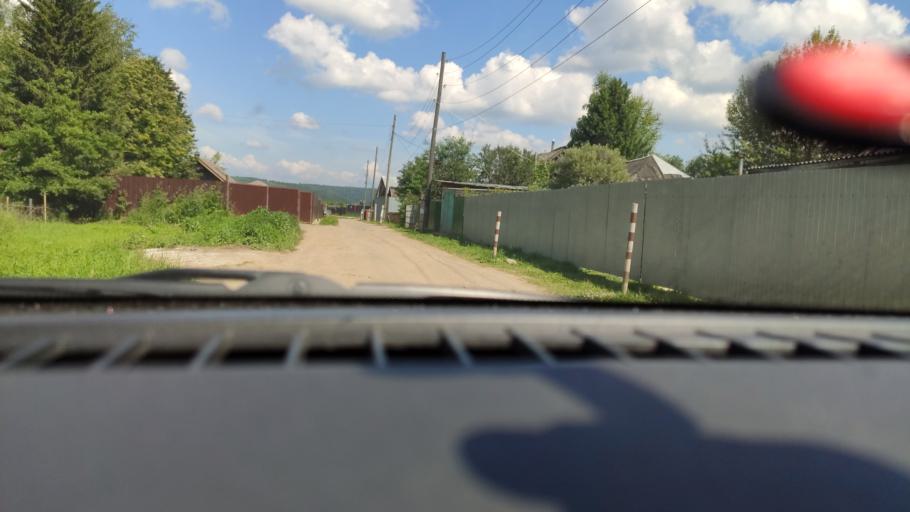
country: RU
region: Perm
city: Sylva
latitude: 58.0467
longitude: 56.7258
